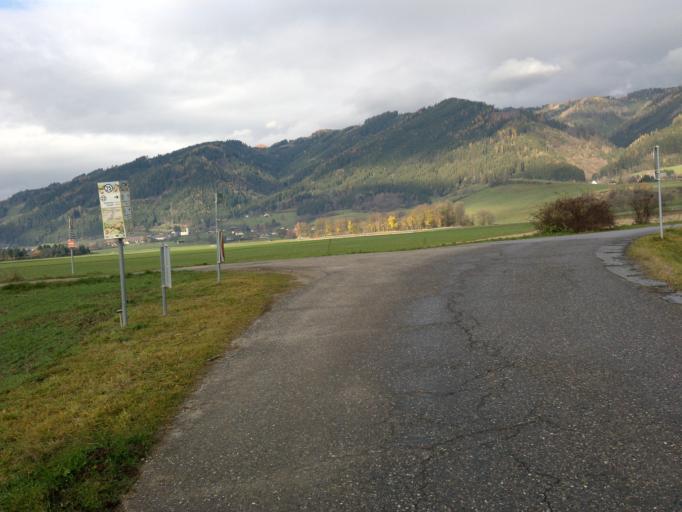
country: AT
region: Styria
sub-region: Politischer Bezirk Murtal
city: Flatschach
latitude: 47.2086
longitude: 14.7217
